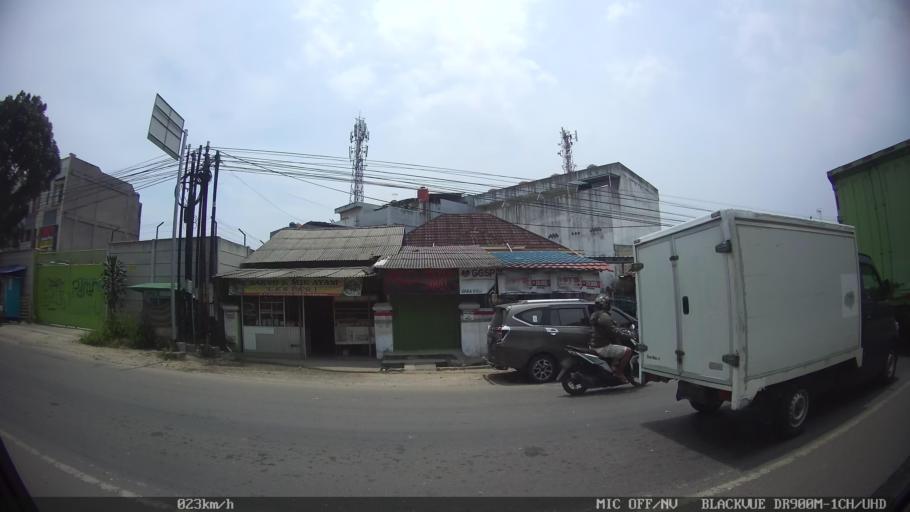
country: ID
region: Lampung
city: Kedaton
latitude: -5.3950
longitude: 105.2964
